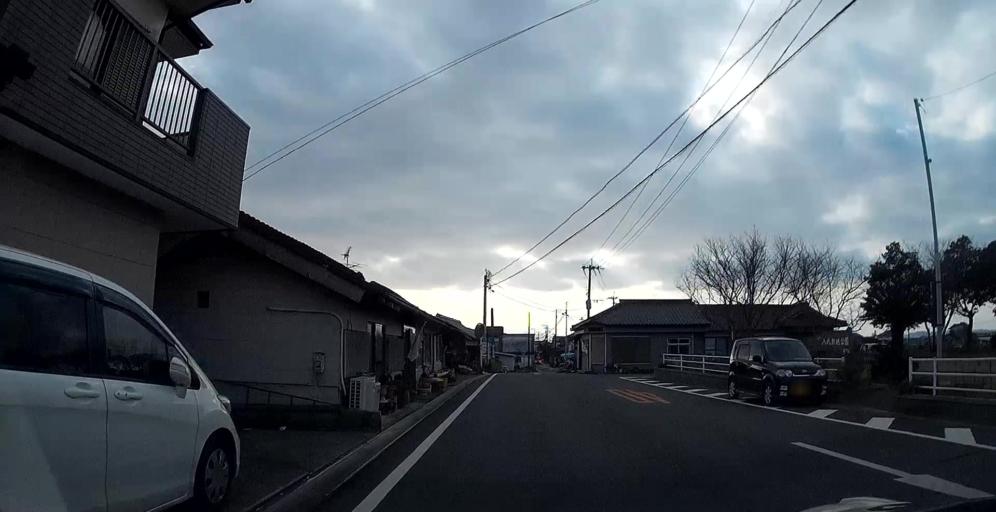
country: JP
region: Kumamoto
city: Yatsushiro
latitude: 32.5517
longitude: 130.6209
